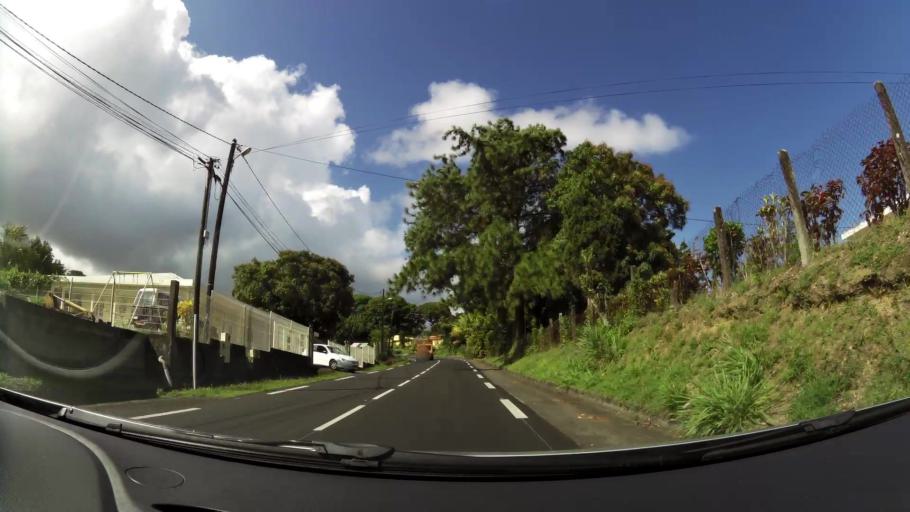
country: MQ
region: Martinique
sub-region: Martinique
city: Basse-Pointe
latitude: 14.8317
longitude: -61.1038
